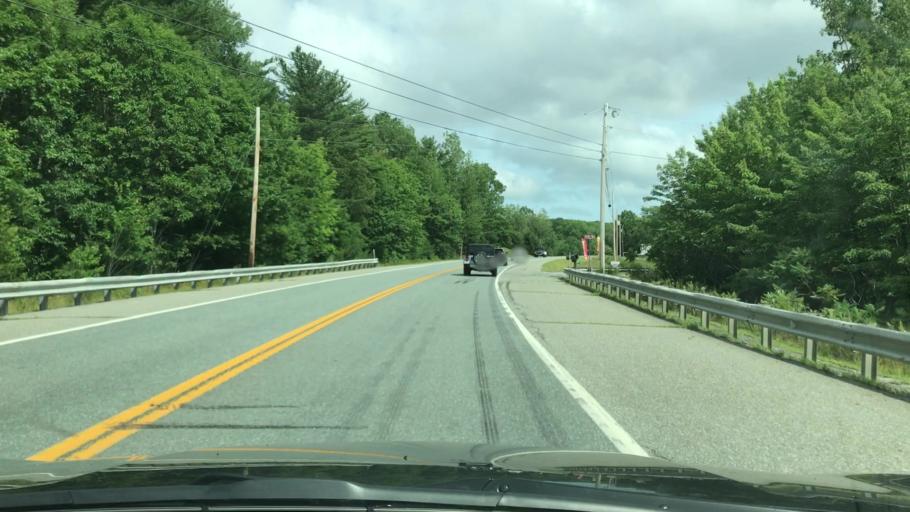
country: US
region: Maine
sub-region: Hancock County
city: Surry
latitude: 44.5632
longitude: -68.5892
